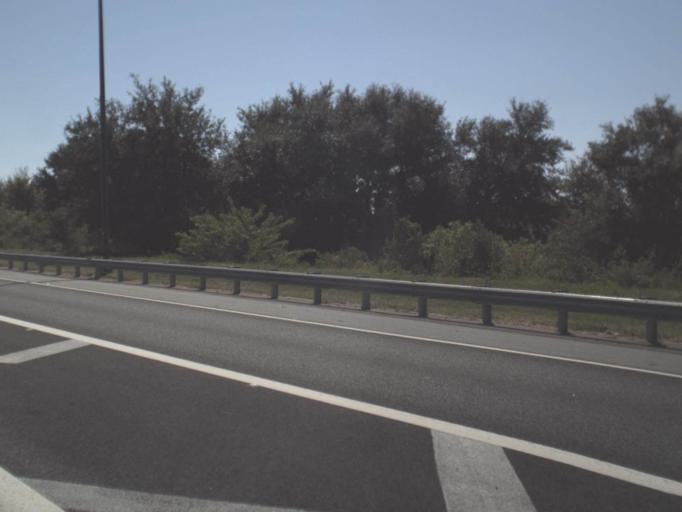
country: US
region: Florida
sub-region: Lake County
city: Hawthorne
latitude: 28.7514
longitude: -81.9347
